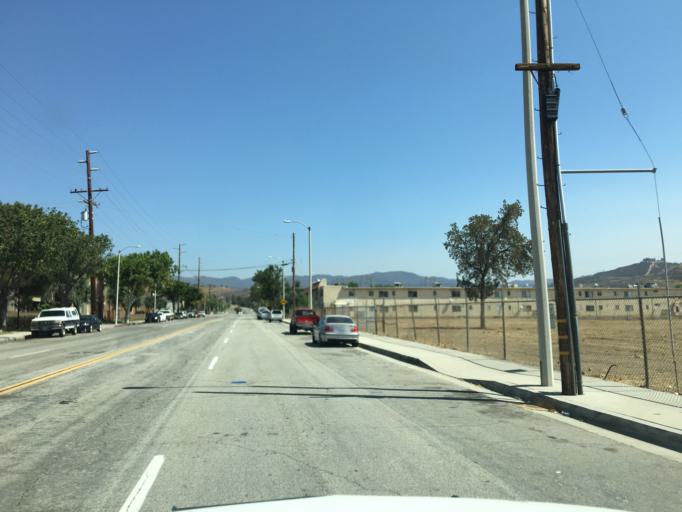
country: US
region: California
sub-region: Los Angeles County
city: Castaic
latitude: 34.4944
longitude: -118.6166
